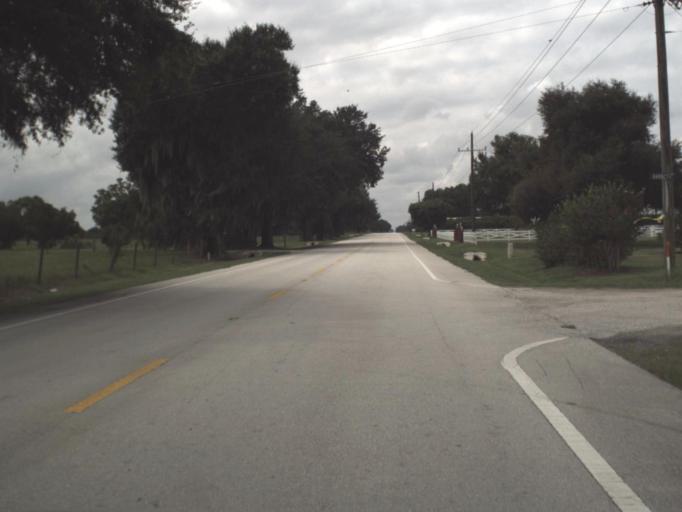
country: US
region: Florida
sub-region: Hardee County
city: Bowling Green
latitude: 27.5948
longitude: -81.8914
